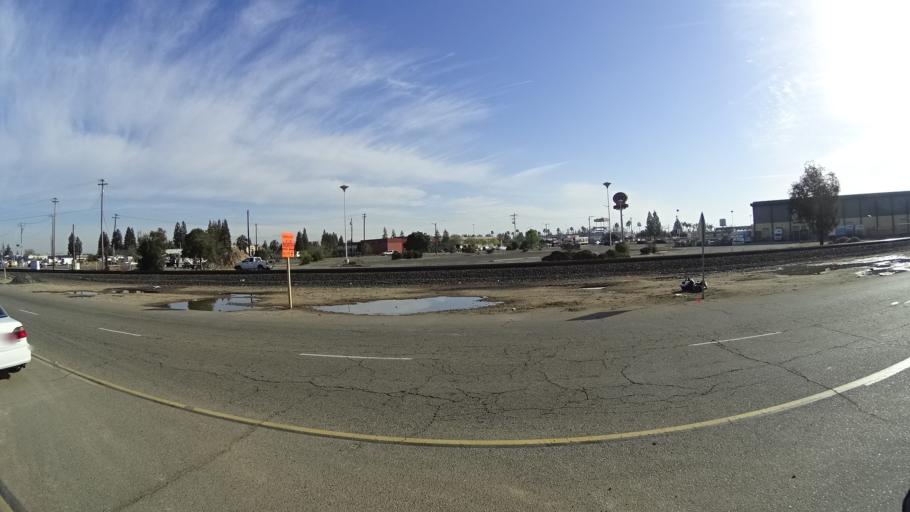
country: US
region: California
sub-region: Fresno County
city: West Park
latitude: 36.8072
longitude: -119.8766
